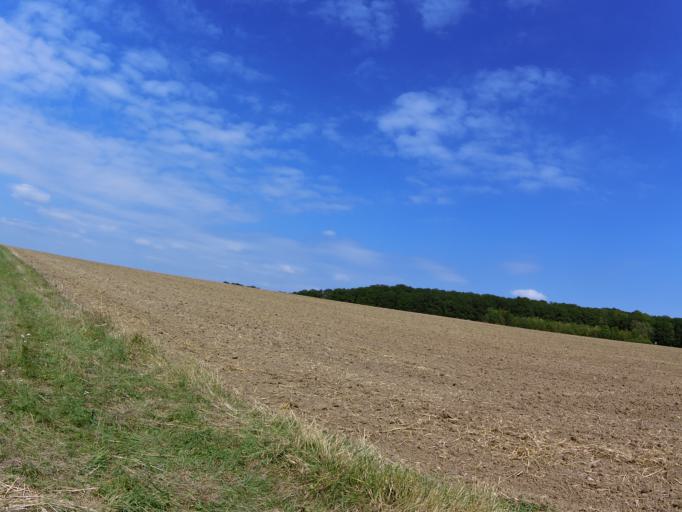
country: DE
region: Bavaria
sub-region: Regierungsbezirk Unterfranken
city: Waldbrunn
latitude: 49.7117
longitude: 9.7982
